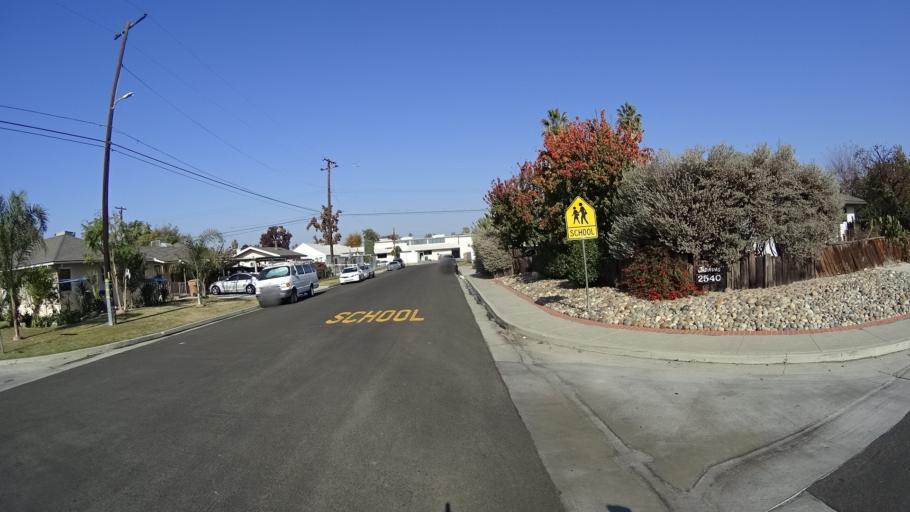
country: US
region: California
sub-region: Kern County
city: Bakersfield
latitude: 35.3431
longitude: -119.0322
